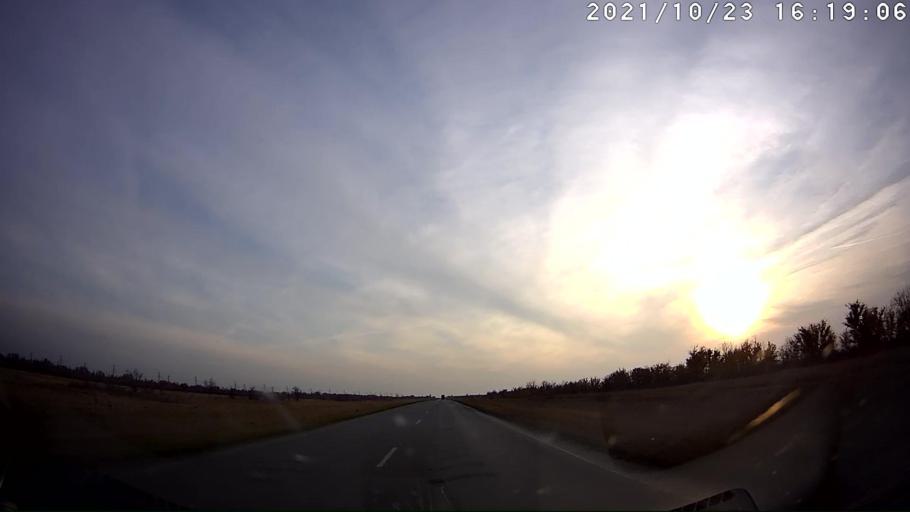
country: RU
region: Volgograd
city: Kotel'nikovo
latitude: 47.8915
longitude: 43.5416
